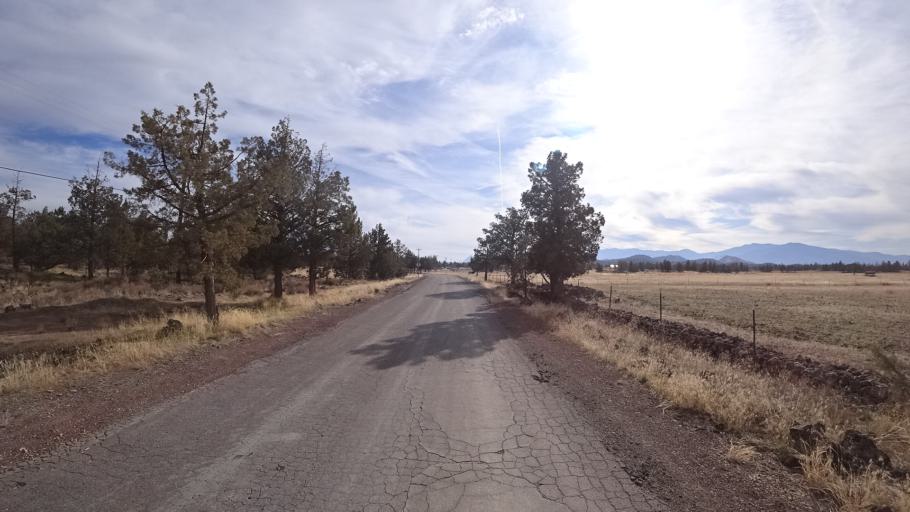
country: US
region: California
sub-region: Siskiyou County
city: Weed
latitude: 41.5950
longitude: -122.4031
